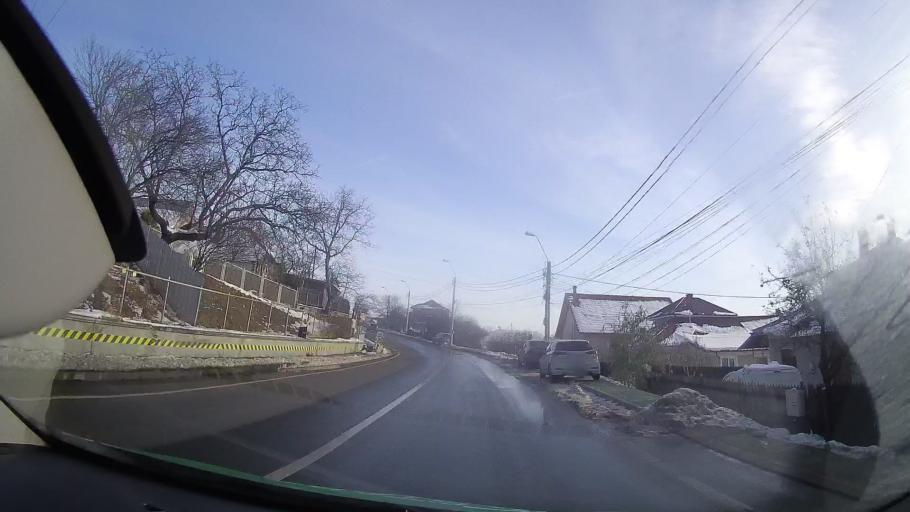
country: RO
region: Neamt
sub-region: Comuna Garcina
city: Garcina
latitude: 46.9725
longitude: 26.3670
